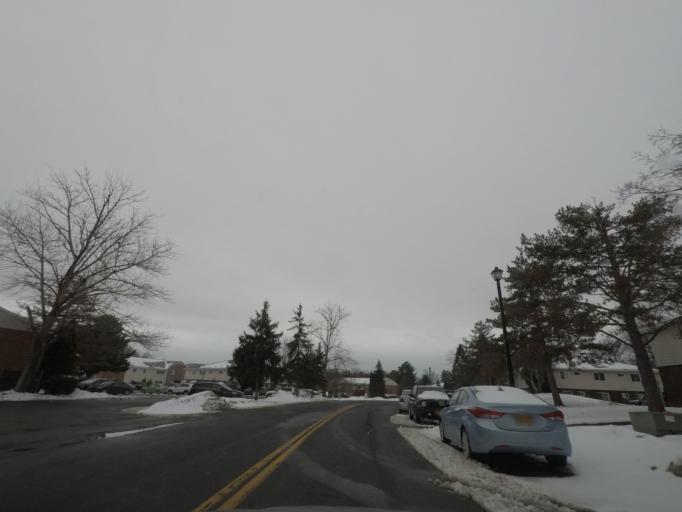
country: US
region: New York
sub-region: Albany County
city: Watervliet
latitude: 42.7313
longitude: -73.7297
